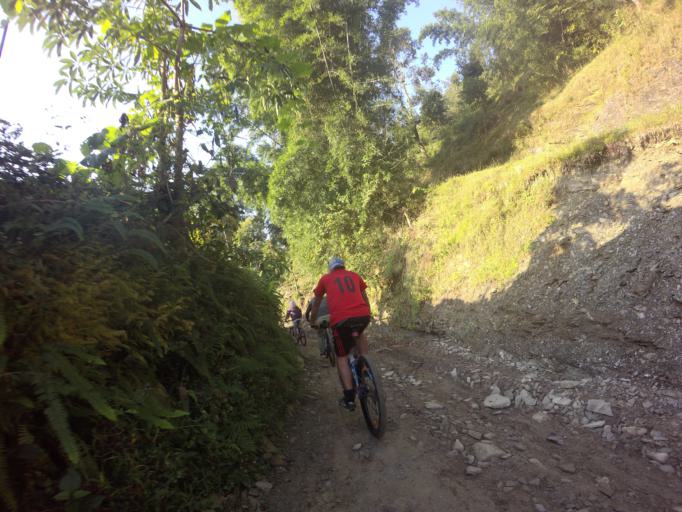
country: NP
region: Western Region
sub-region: Gandaki Zone
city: Pokhara
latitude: 28.2527
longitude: 84.0074
